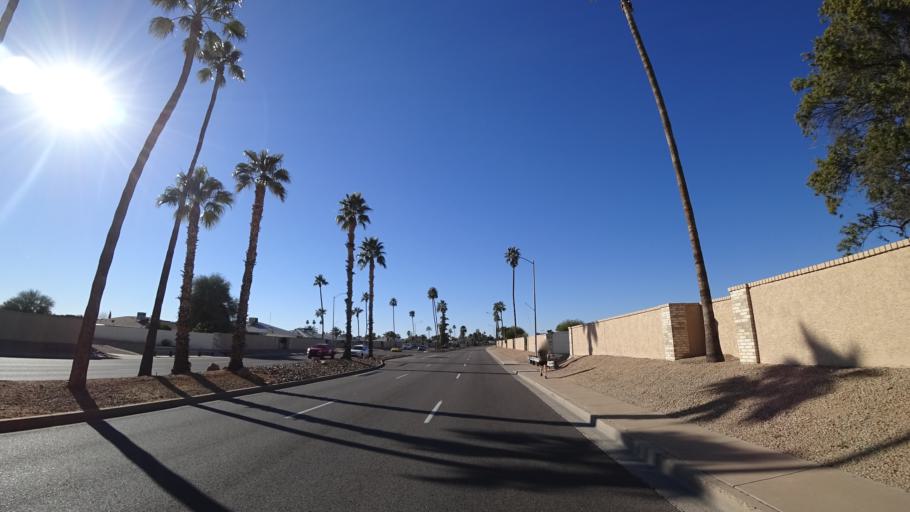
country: US
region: Arizona
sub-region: Maricopa County
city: Sun City West
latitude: 33.6520
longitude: -112.3421
